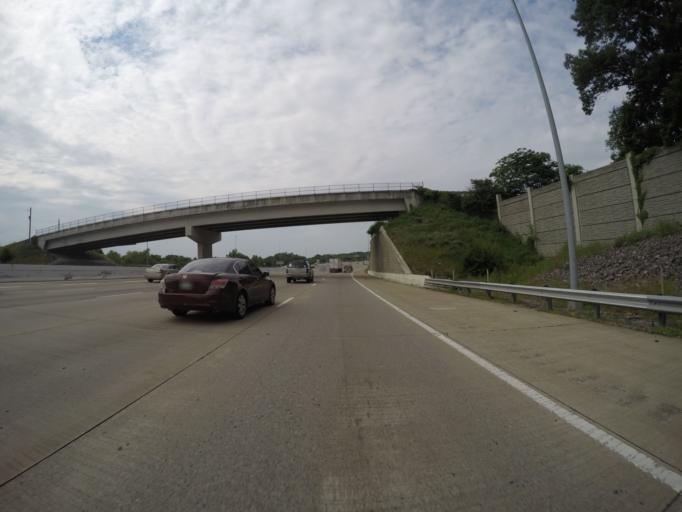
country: US
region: Tennessee
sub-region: Davidson County
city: Goodlettsville
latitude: 36.2561
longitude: -86.7387
